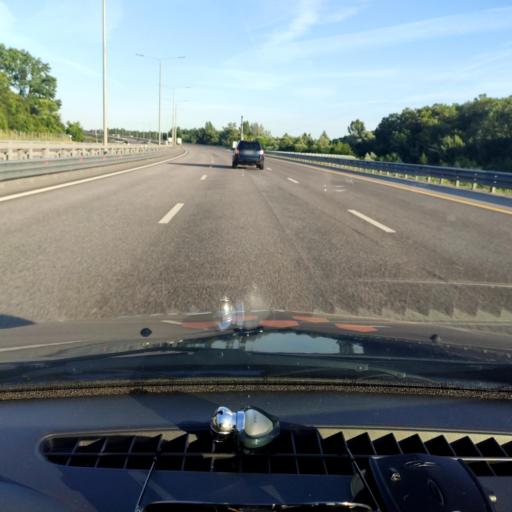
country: RU
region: Voronezj
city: Podgornoye
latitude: 51.7986
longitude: 39.2554
